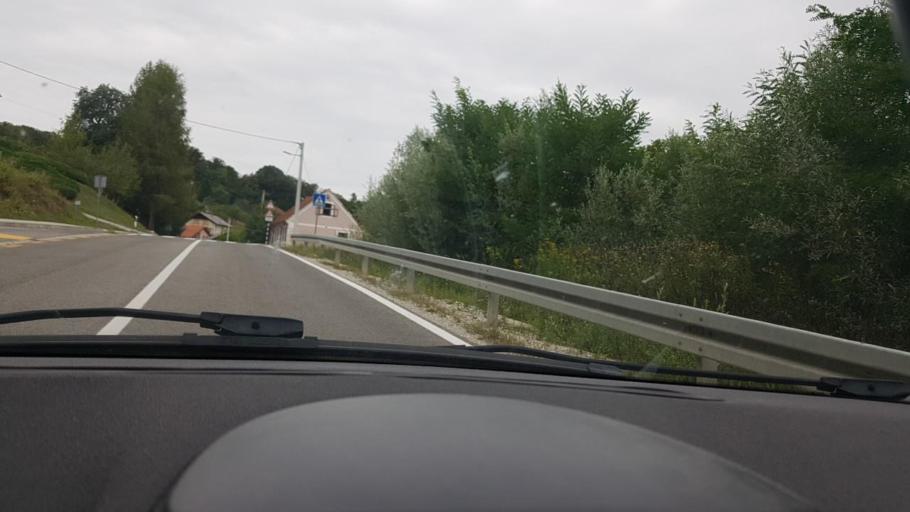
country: SI
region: Rogatec
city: Rogatec
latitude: 46.2057
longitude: 15.6918
